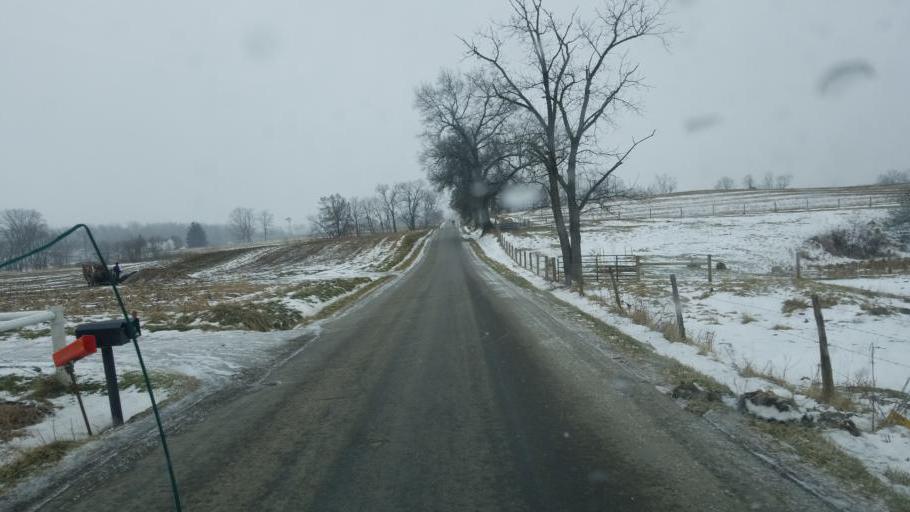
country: US
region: Ohio
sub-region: Wayne County
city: Apple Creek
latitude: 40.6784
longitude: -81.8422
